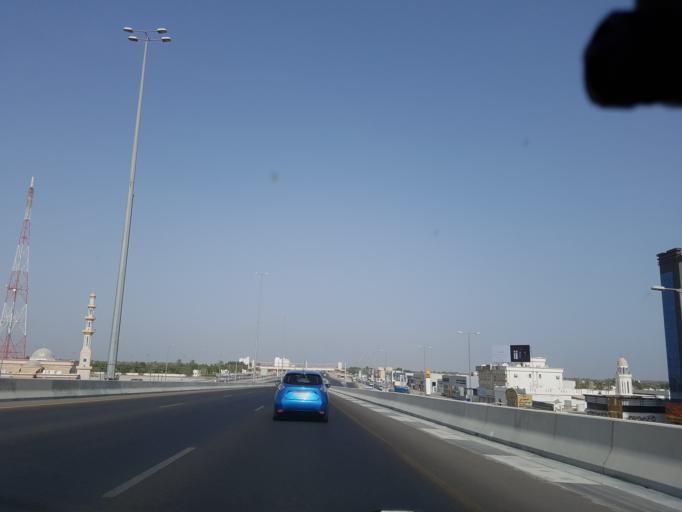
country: OM
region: Al Batinah
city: Barka'
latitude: 23.6679
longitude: 57.8810
